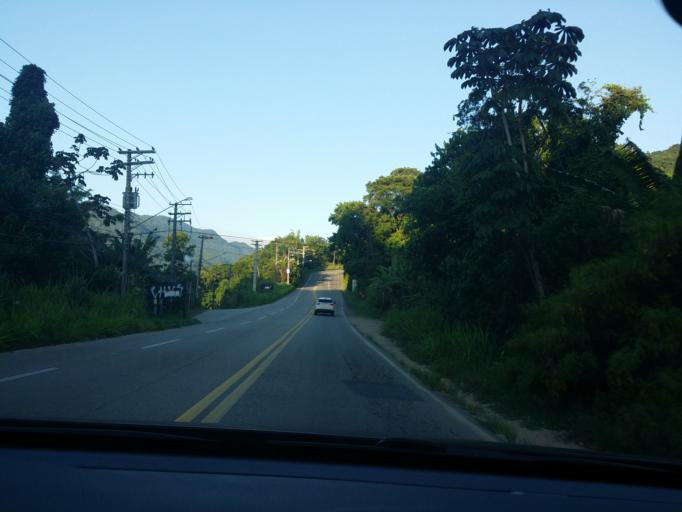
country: BR
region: Sao Paulo
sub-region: Sao Sebastiao
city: Sao Sebastiao
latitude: -23.7841
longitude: -45.6165
